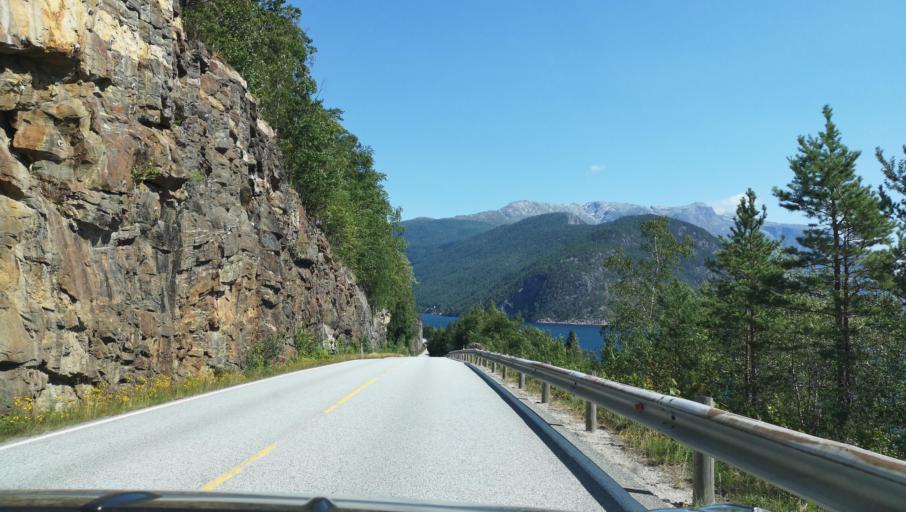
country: NO
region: Hordaland
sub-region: Ulvik
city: Ulvik
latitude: 60.4875
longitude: 6.8838
